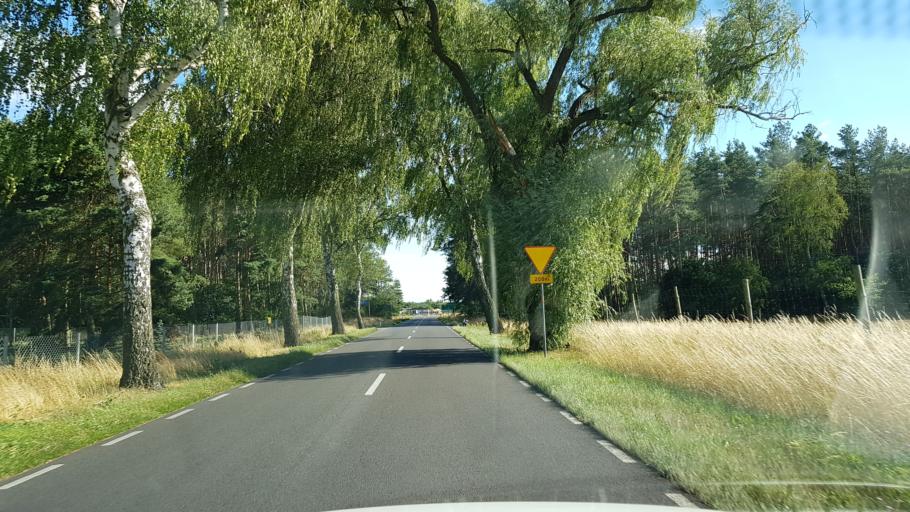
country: PL
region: West Pomeranian Voivodeship
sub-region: Powiat goleniowski
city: Goleniow
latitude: 53.5809
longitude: 14.7409
